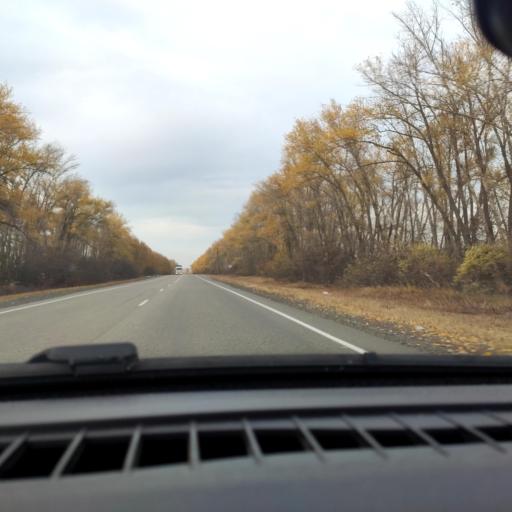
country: RU
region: Voronezj
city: Ostrogozhsk
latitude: 50.9908
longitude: 38.9979
